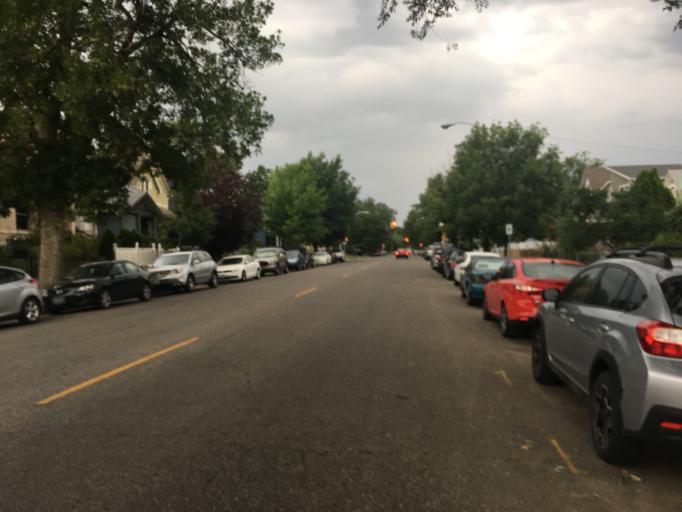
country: US
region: Colorado
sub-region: Denver County
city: Denver
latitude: 39.7629
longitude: -104.9660
